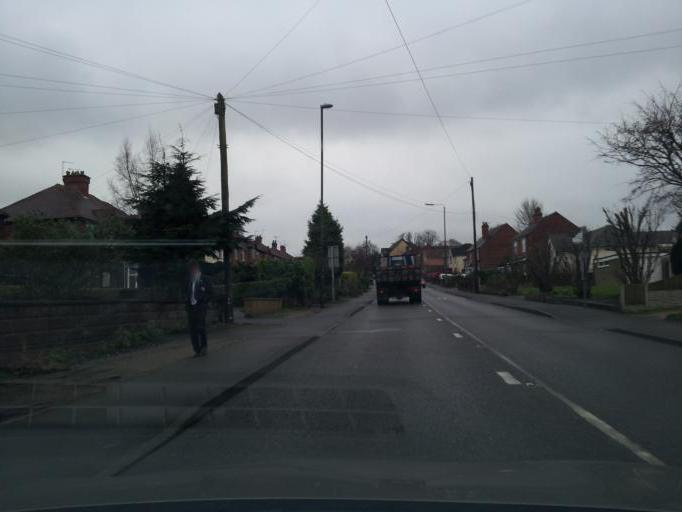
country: GB
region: England
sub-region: Derbyshire
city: Swadlincote
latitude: 52.7758
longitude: -1.5385
